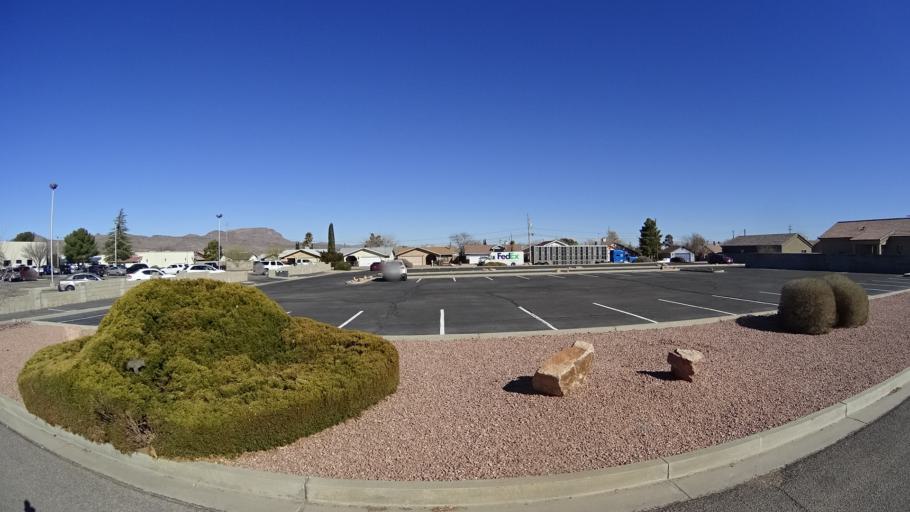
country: US
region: Arizona
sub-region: Mohave County
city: Kingman
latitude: 35.2067
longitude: -114.0324
